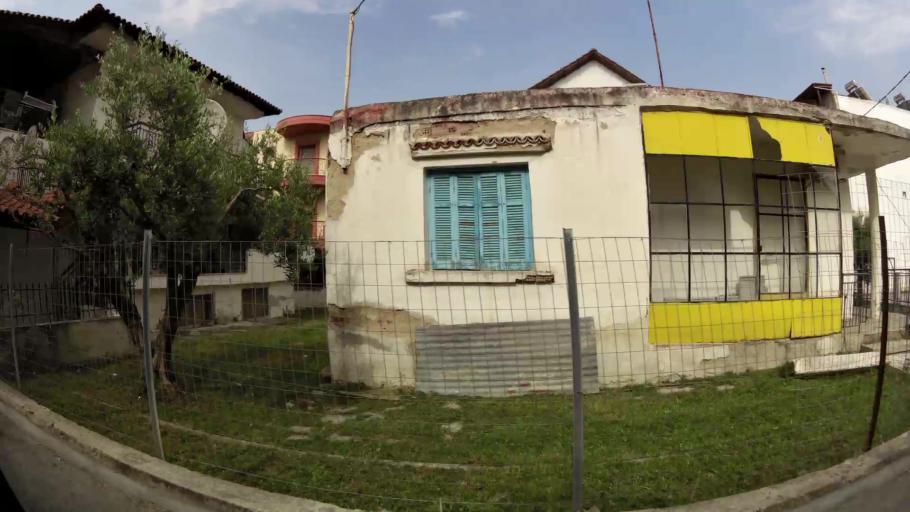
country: GR
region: Central Macedonia
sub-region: Nomos Thessalonikis
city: Stavroupoli
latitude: 40.6813
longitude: 22.9366
